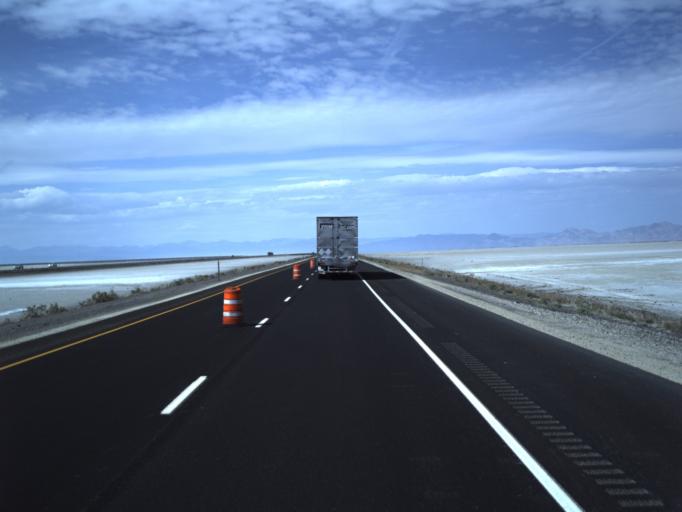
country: US
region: Utah
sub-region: Tooele County
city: Wendover
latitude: 40.7335
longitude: -113.5751
